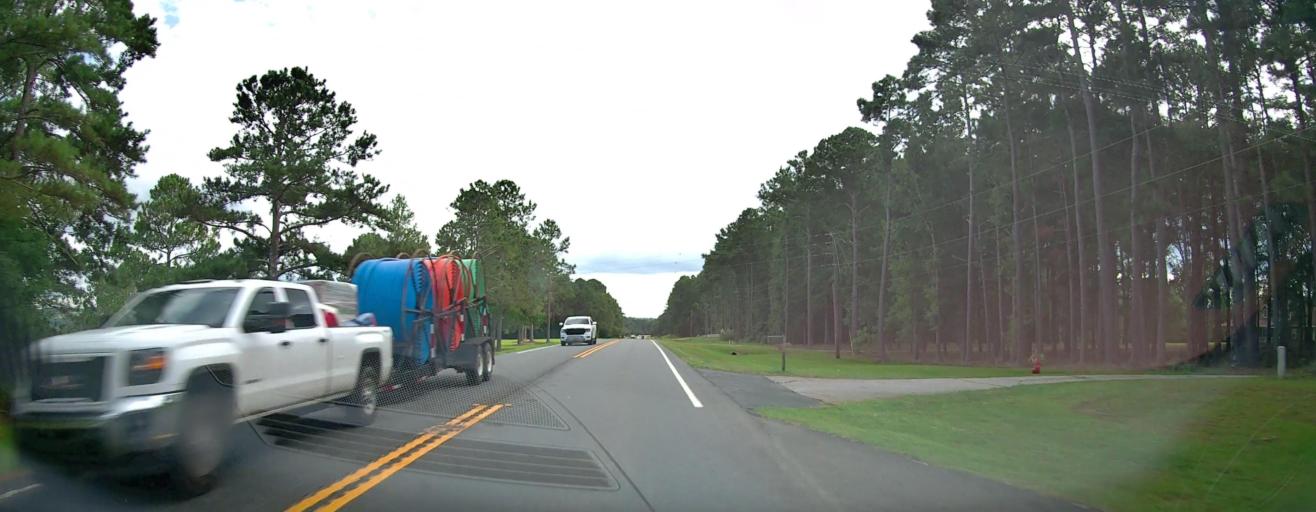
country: US
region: Georgia
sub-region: Meriwether County
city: Manchester
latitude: 32.9740
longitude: -84.5997
